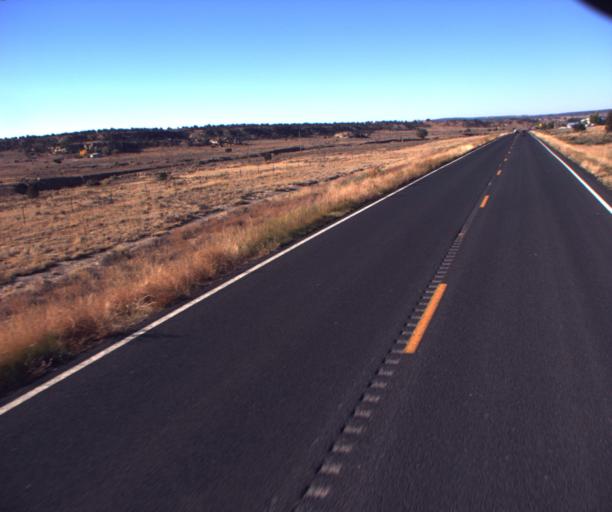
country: US
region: Arizona
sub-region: Apache County
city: Ganado
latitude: 35.7506
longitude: -109.8452
